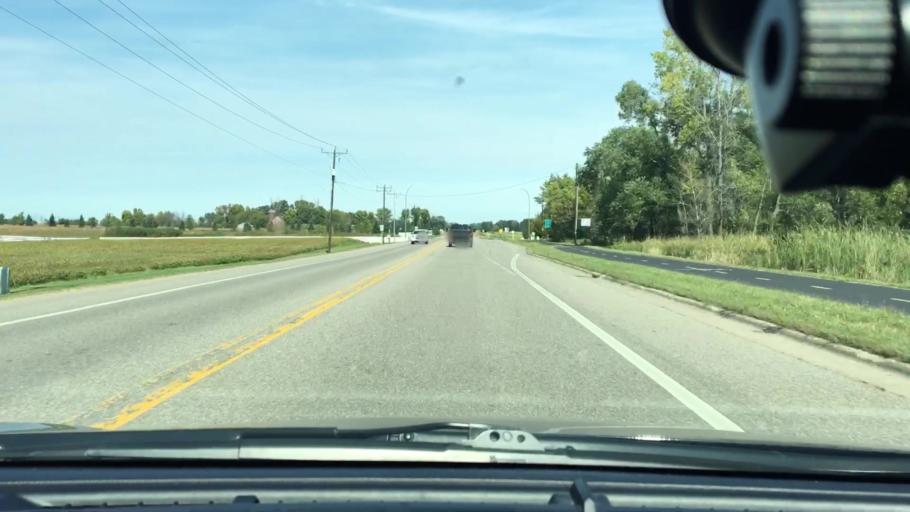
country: US
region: Minnesota
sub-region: Wright County
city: Hanover
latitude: 45.1292
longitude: -93.6357
